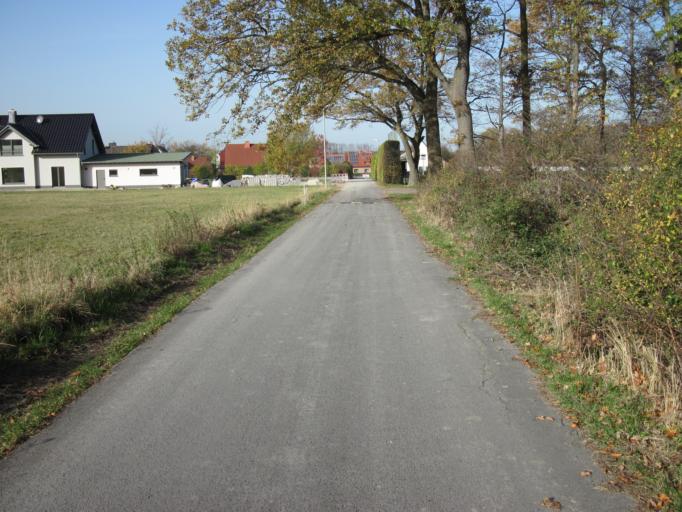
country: DE
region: North Rhine-Westphalia
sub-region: Regierungsbezirk Detmold
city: Salzkotten
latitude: 51.6060
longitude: 8.6655
